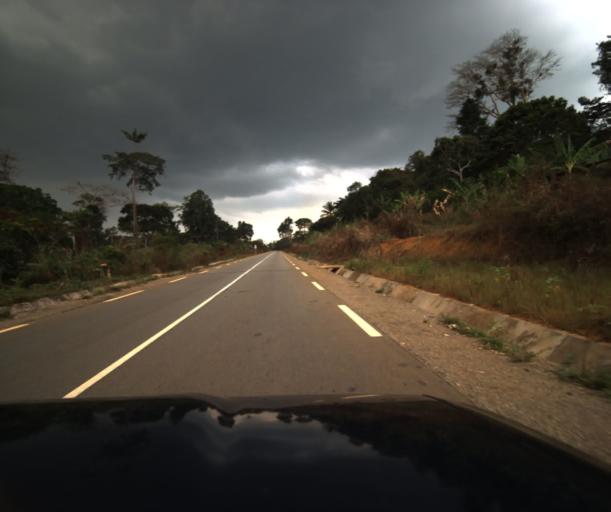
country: CM
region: Centre
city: Mbankomo
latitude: 3.6731
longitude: 11.3498
